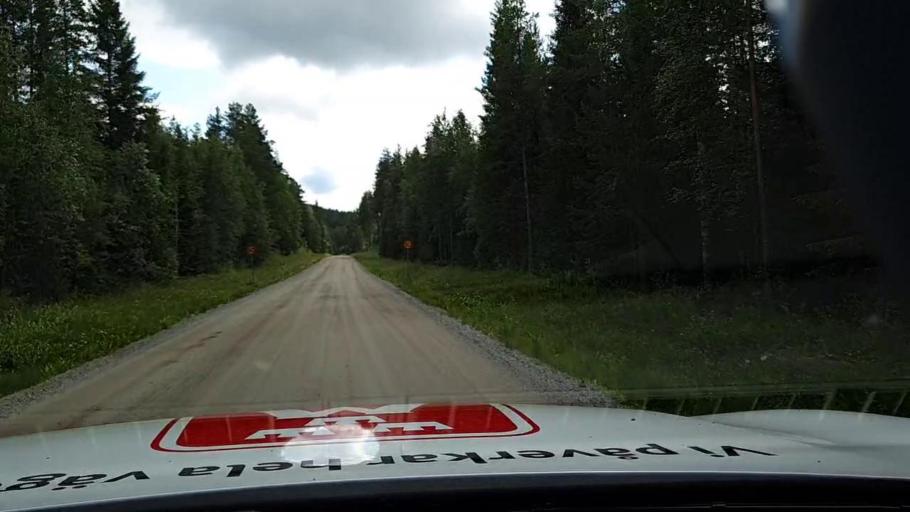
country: SE
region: Jaemtland
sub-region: Braecke Kommun
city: Braecke
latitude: 62.7808
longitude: 15.4717
